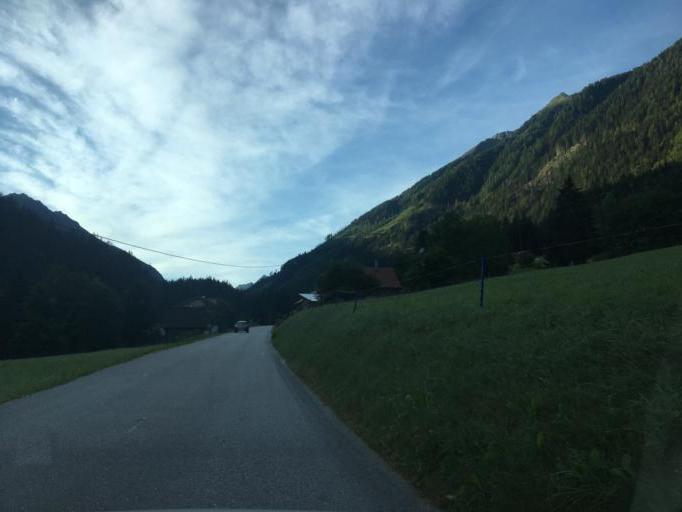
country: AT
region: Styria
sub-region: Politischer Bezirk Liezen
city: Schladming
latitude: 47.3624
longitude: 13.6864
